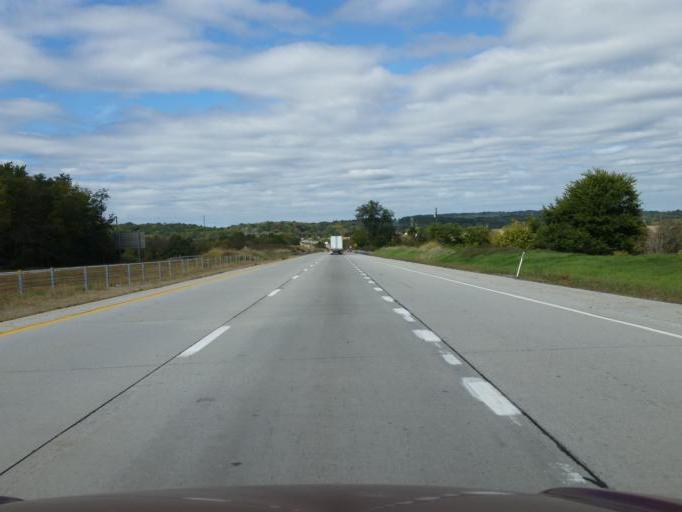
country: US
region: Pennsylvania
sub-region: Lancaster County
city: Elizabethtown
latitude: 40.1813
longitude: -76.6048
